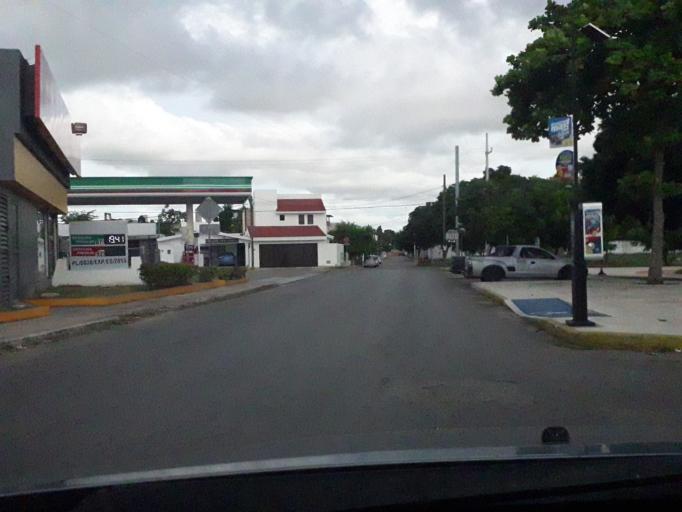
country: MX
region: Yucatan
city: Merida
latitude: 21.0204
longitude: -89.6358
